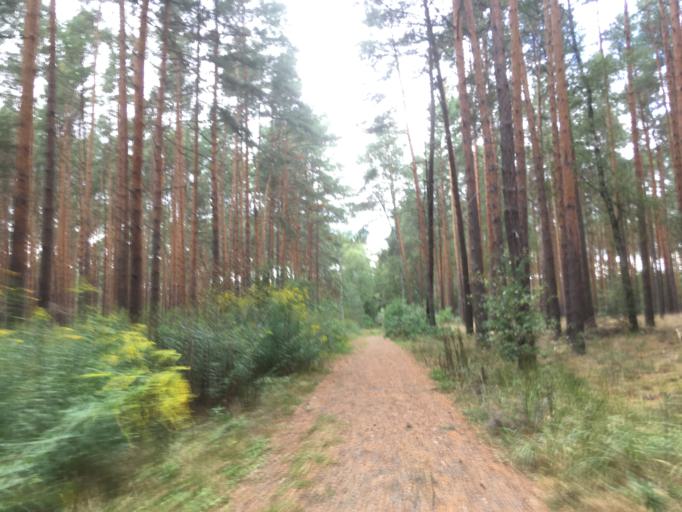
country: DE
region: Brandenburg
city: Wildau
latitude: 52.3189
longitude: 13.6999
